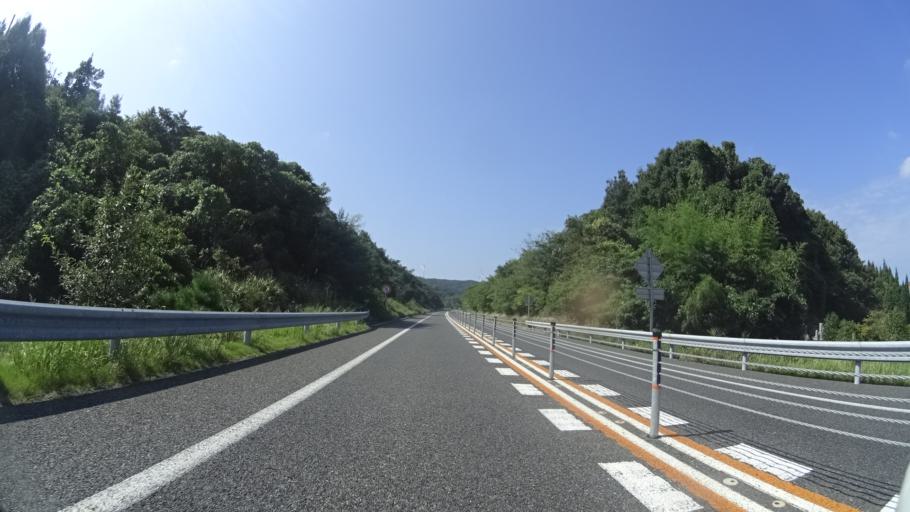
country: JP
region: Shimane
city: Gotsucho
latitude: 34.9765
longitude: 132.1956
